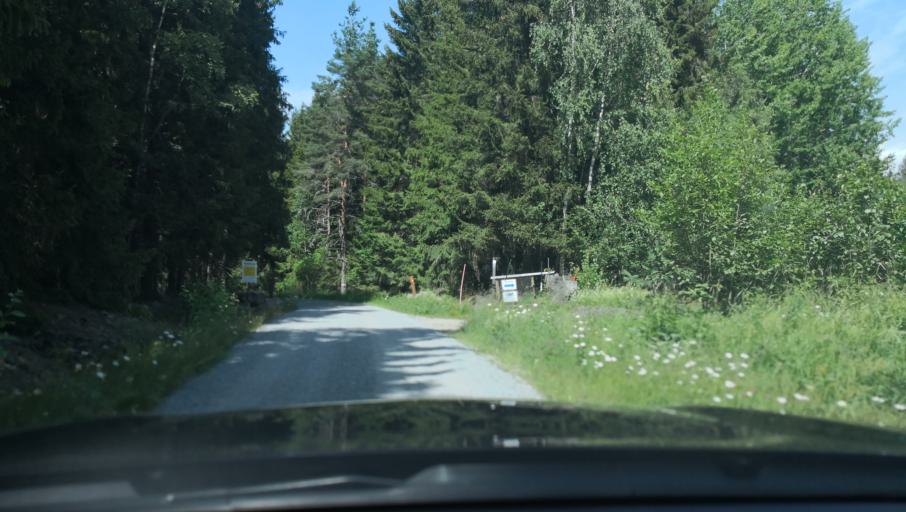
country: SE
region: Vaestmanland
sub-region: Surahammars Kommun
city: Ramnas
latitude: 59.8802
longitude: 16.0937
